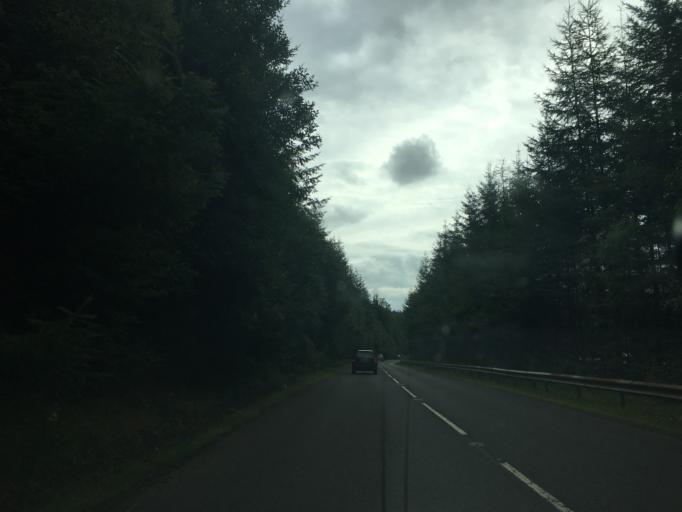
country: GB
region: Scotland
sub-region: Stirling
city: Callander
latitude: 56.2889
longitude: -4.2843
